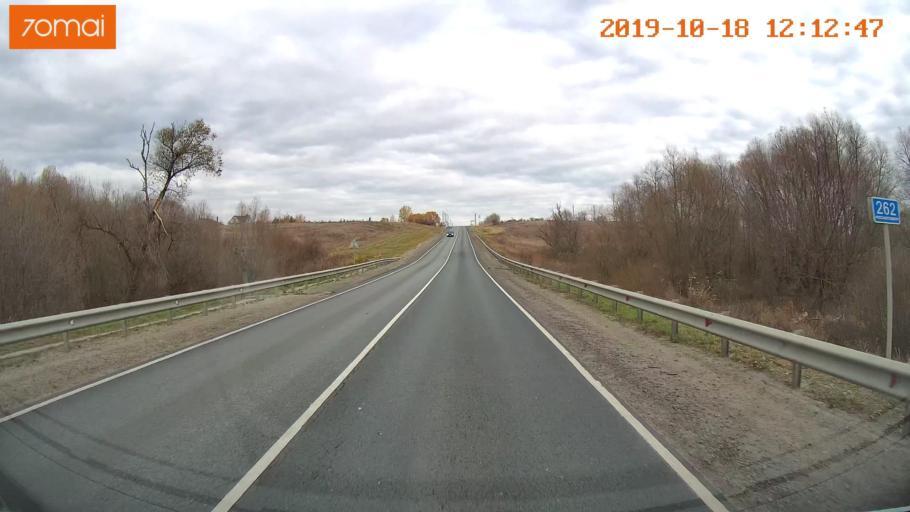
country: RU
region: Rjazan
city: Zakharovo
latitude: 54.4153
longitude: 39.3623
